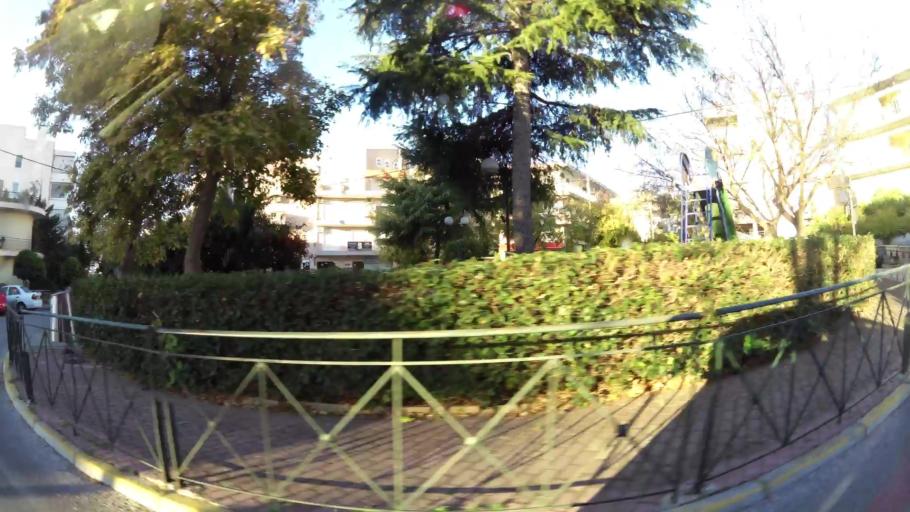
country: GR
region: Attica
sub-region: Nomarchia Anatolikis Attikis
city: Pallini
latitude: 38.0021
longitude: 23.8768
